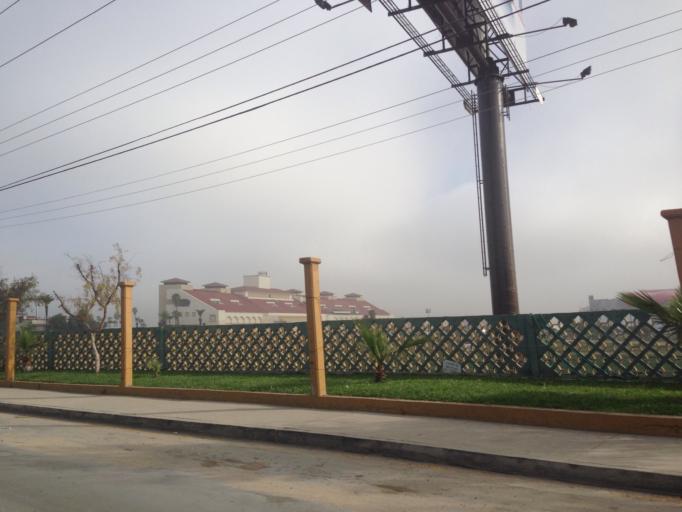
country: MX
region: Baja California
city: Tijuana
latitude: 32.5045
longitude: -116.9986
